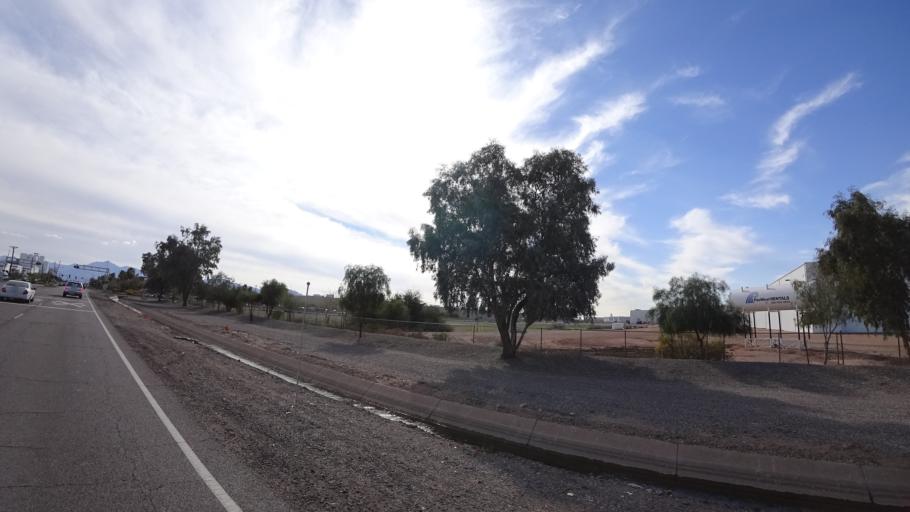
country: US
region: Arizona
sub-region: Maricopa County
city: Tolleson
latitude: 33.4443
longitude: -112.2725
